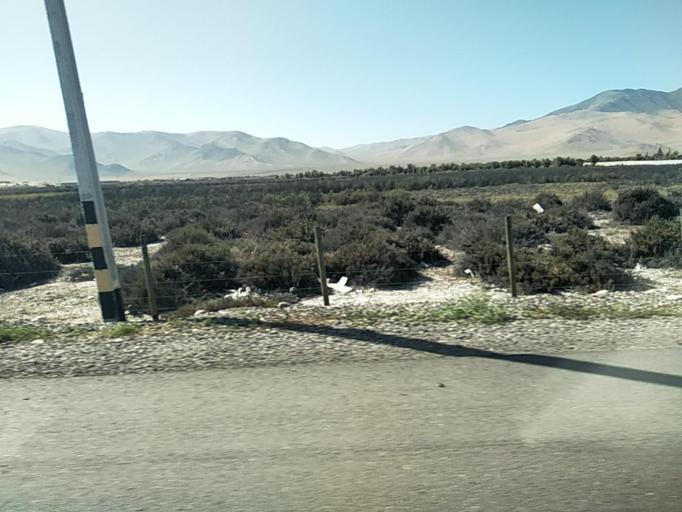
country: CL
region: Atacama
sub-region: Provincia de Copiapo
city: Copiapo
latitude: -27.3420
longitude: -70.6136
